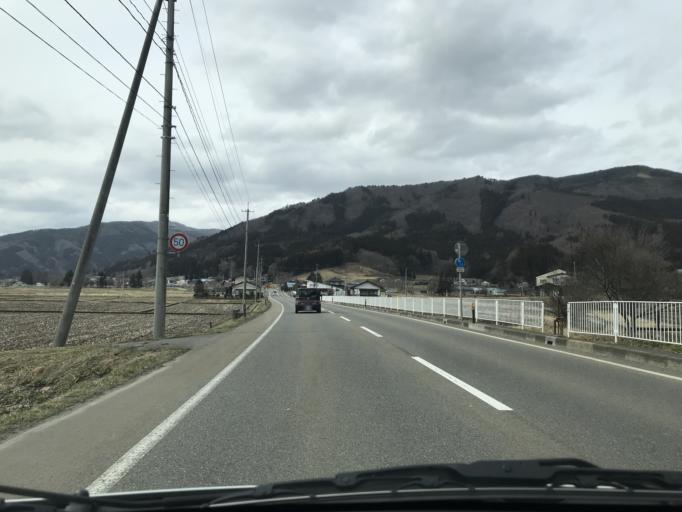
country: JP
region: Iwate
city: Tono
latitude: 39.3318
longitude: 141.4777
